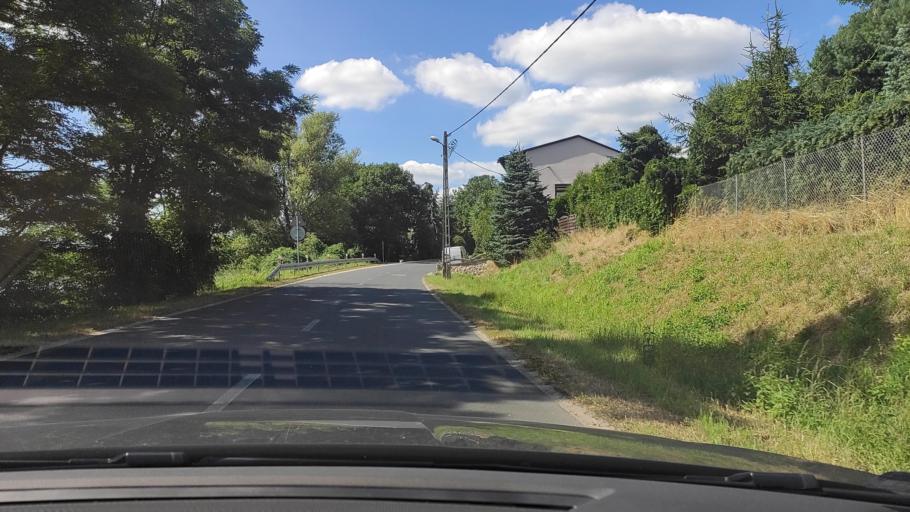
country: PL
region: Greater Poland Voivodeship
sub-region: Powiat poznanski
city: Kostrzyn
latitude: 52.4781
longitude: 17.1800
